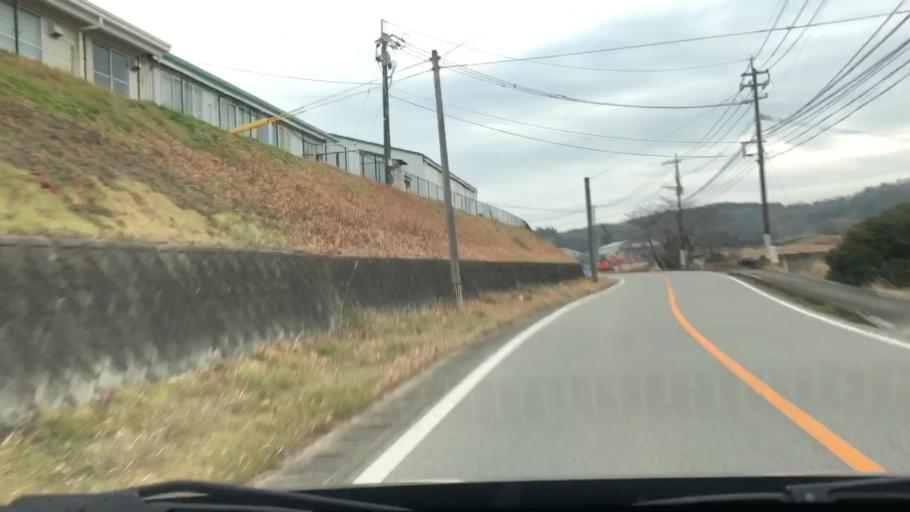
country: JP
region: Oita
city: Usuki
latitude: 33.0189
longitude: 131.6727
